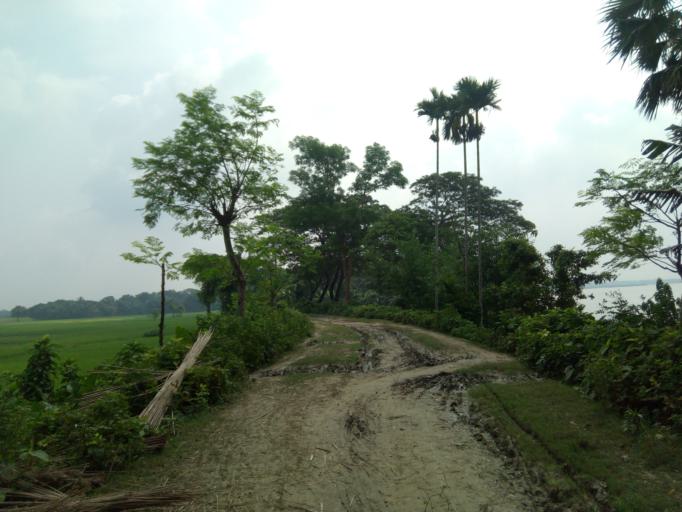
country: BD
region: Khulna
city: Kalia
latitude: 23.0590
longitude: 89.6525
